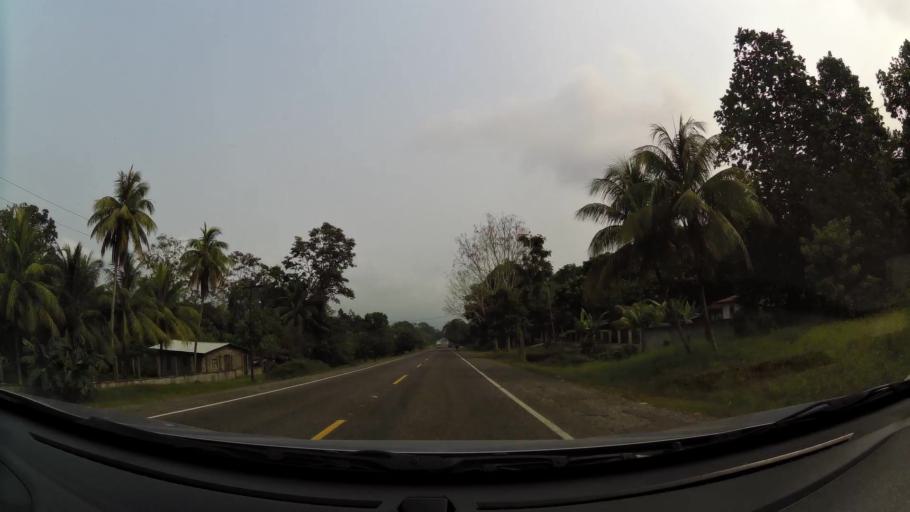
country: HN
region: Atlantida
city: Mezapa
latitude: 15.6002
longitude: -87.6099
